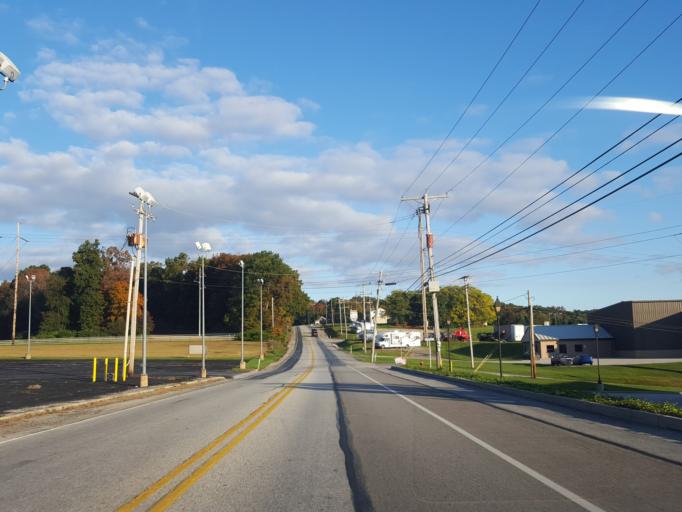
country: US
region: Pennsylvania
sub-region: York County
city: Yoe
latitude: 39.9251
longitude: -76.6358
